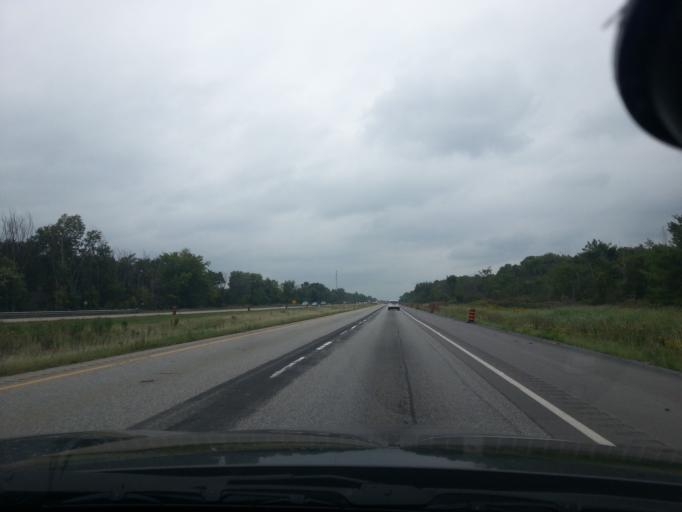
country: US
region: New York
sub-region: Jefferson County
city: Alexandria Bay
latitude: 44.4592
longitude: -75.8816
